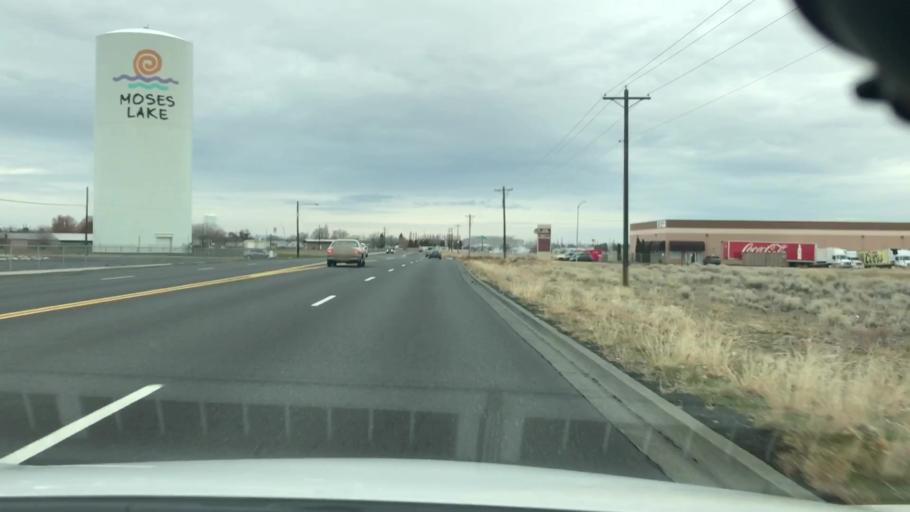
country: US
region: Washington
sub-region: Grant County
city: Moses Lake North
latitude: 47.1700
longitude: -119.3169
